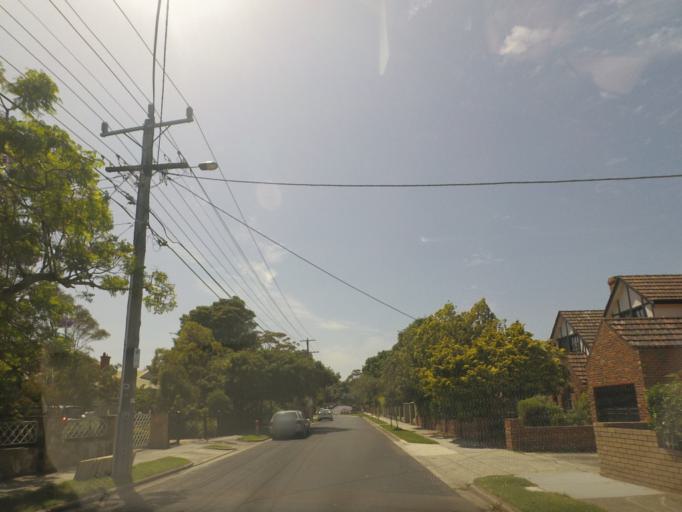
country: AU
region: Victoria
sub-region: Bayside
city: Black Rock
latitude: -37.9614
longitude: 145.0161
